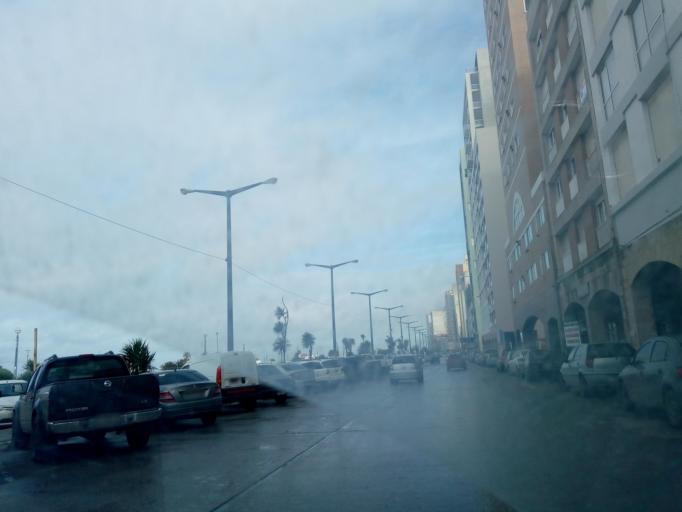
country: AR
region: Buenos Aires
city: Necochea
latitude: -38.5822
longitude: -58.7263
